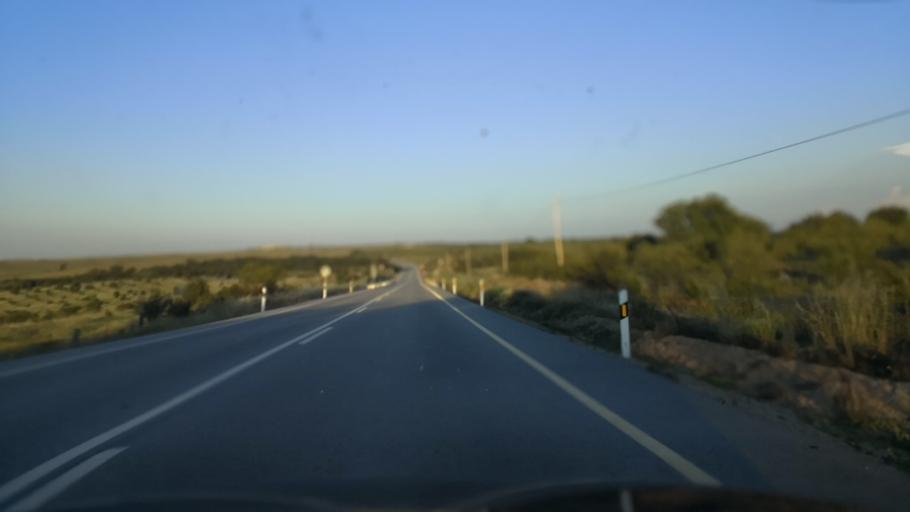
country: ES
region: Extremadura
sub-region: Provincia de Caceres
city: Salorino
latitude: 39.5136
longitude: -7.0728
